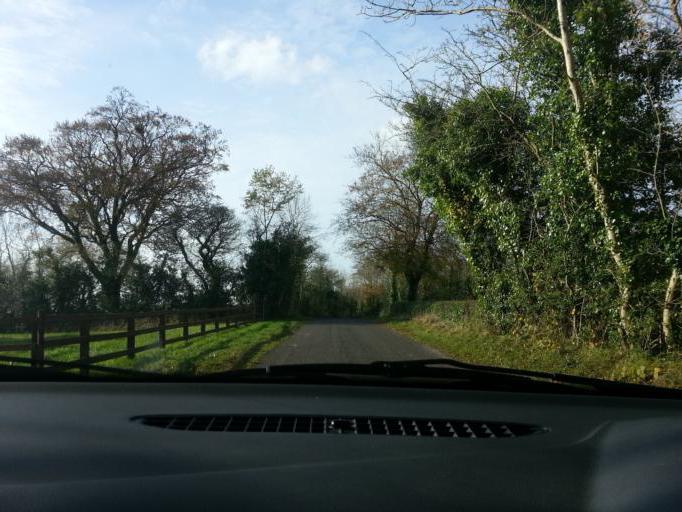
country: IE
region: Ulster
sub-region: County Monaghan
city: Clones
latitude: 54.2285
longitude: -7.2732
